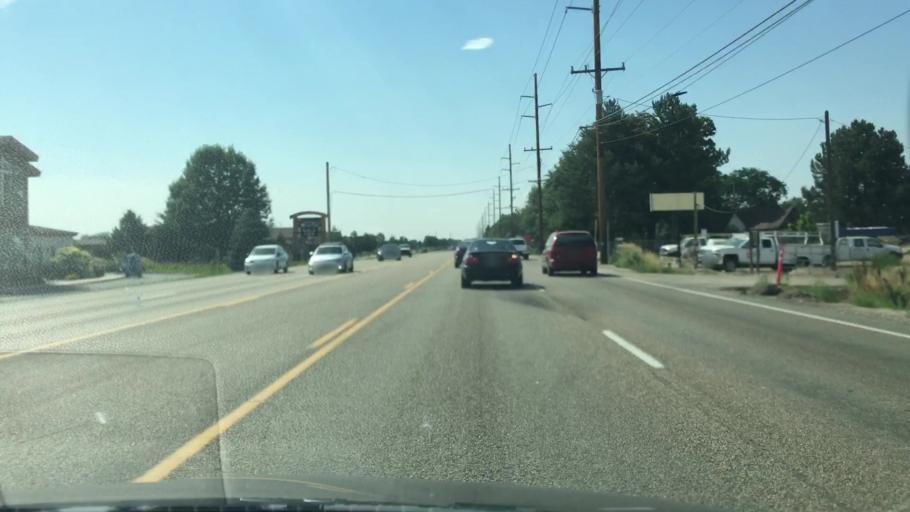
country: US
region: Idaho
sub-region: Ada County
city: Eagle
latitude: 43.6792
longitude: -116.3040
